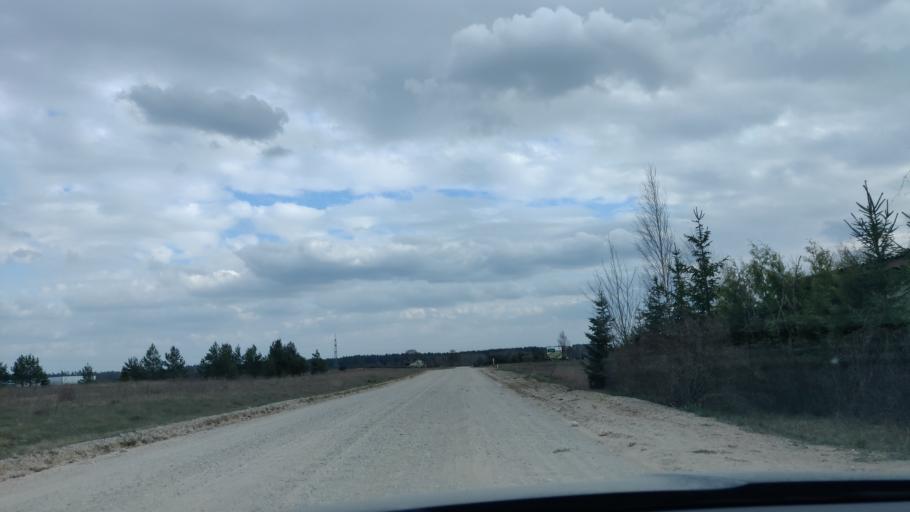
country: LT
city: Lentvaris
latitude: 54.6147
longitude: 25.0687
